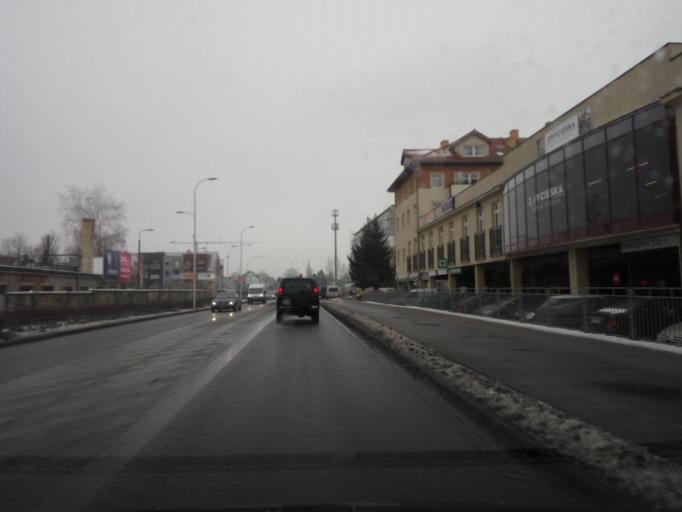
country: PL
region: Lower Silesian Voivodeship
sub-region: Powiat wroclawski
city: Wroclaw
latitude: 51.0588
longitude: 17.0118
